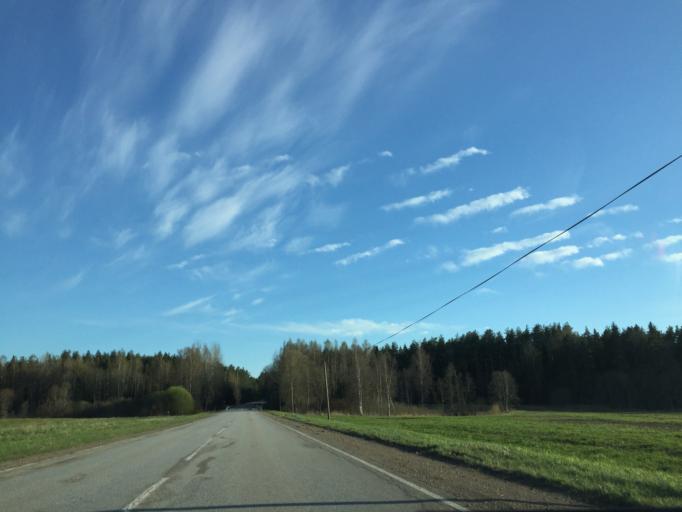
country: LV
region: Valkas Rajons
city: Valka
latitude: 57.7401
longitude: 25.9456
